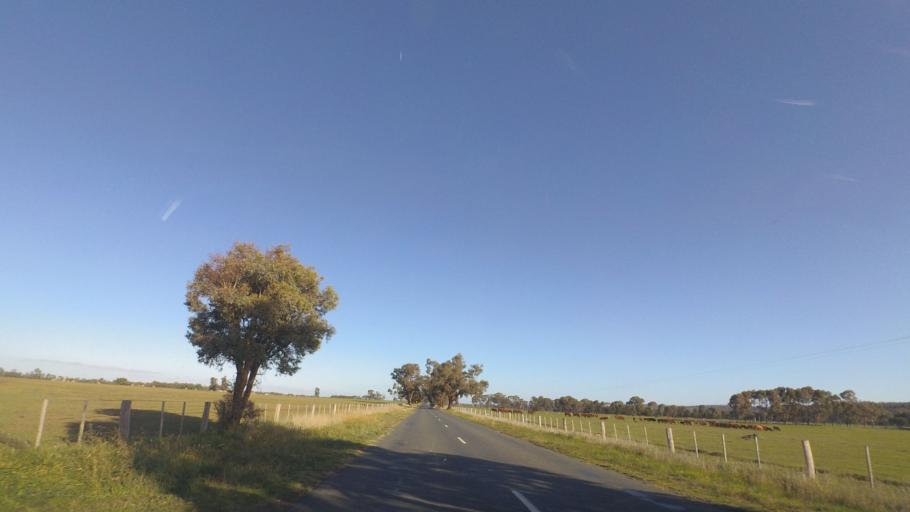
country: AU
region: Victoria
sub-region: Greater Bendigo
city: Epsom
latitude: -36.7060
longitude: 144.5145
